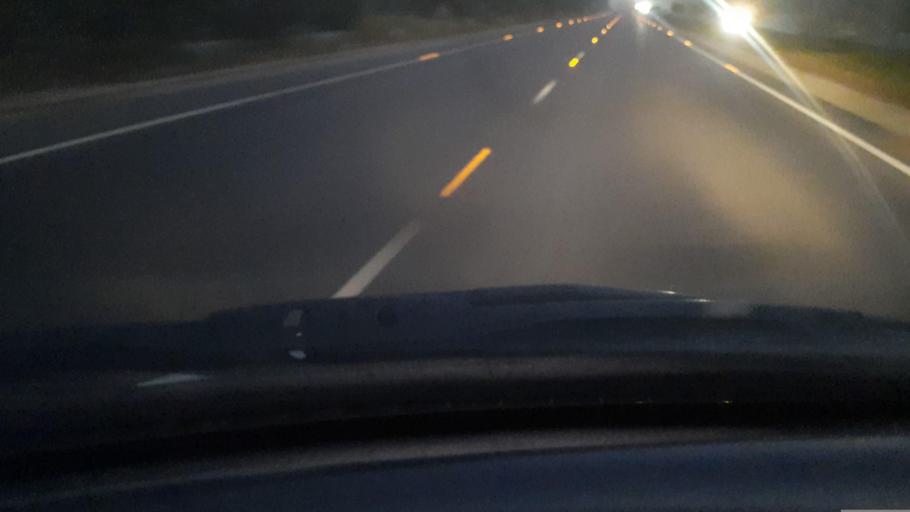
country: BD
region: Dhaka
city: Char Bhadrasan
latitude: 23.4007
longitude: 90.1747
